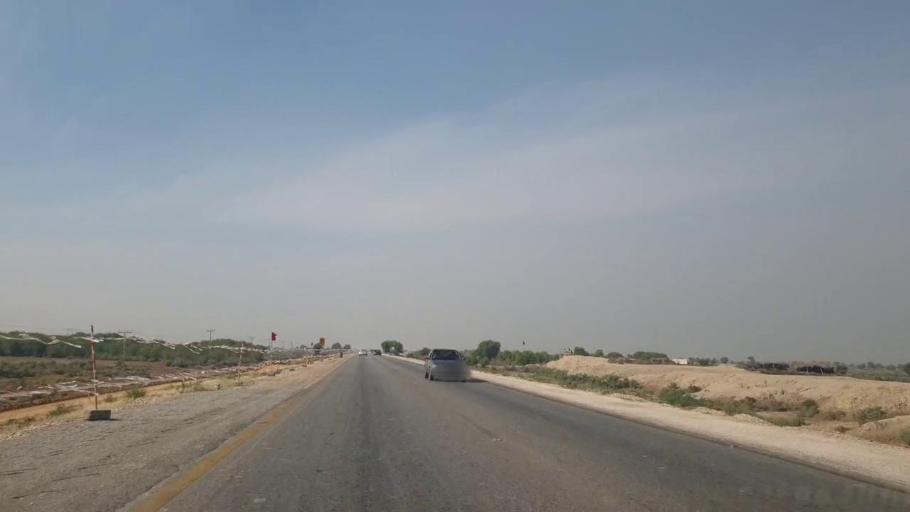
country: PK
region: Sindh
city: Sann
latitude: 25.9942
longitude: 68.1708
